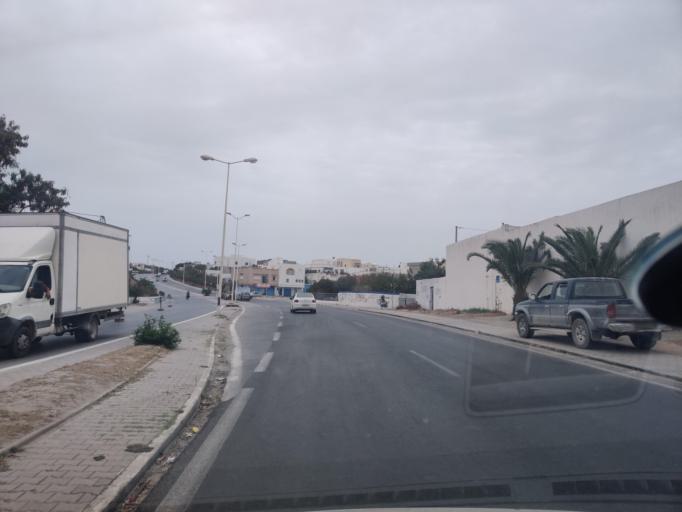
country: TN
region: Nabul
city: Al Hammamat
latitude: 36.4091
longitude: 10.6151
